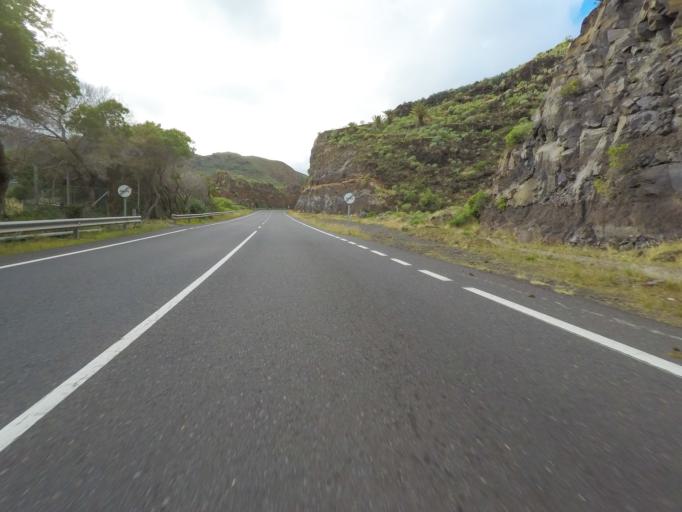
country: ES
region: Canary Islands
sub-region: Provincia de Santa Cruz de Tenerife
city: San Sebastian de la Gomera
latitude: 28.1175
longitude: -17.1398
